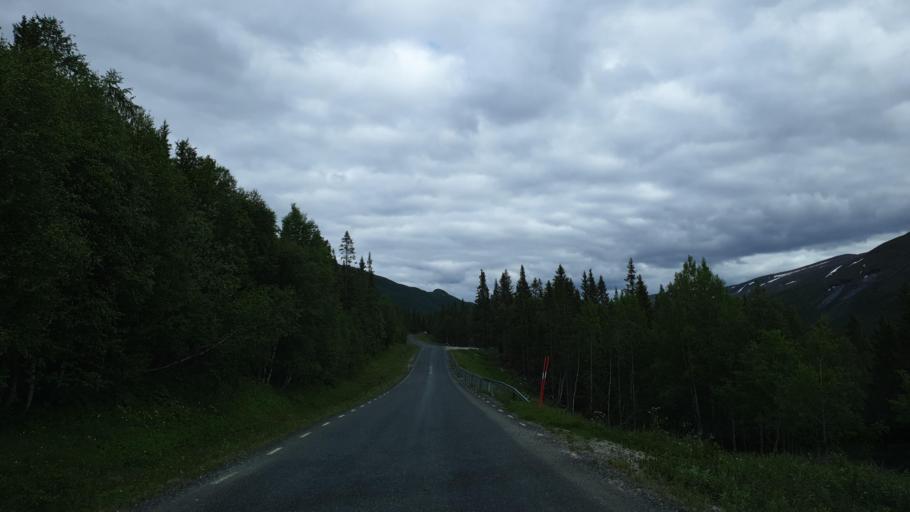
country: NO
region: Nordland
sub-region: Hattfjelldal
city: Hattfjelldal
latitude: 65.4442
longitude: 14.5369
